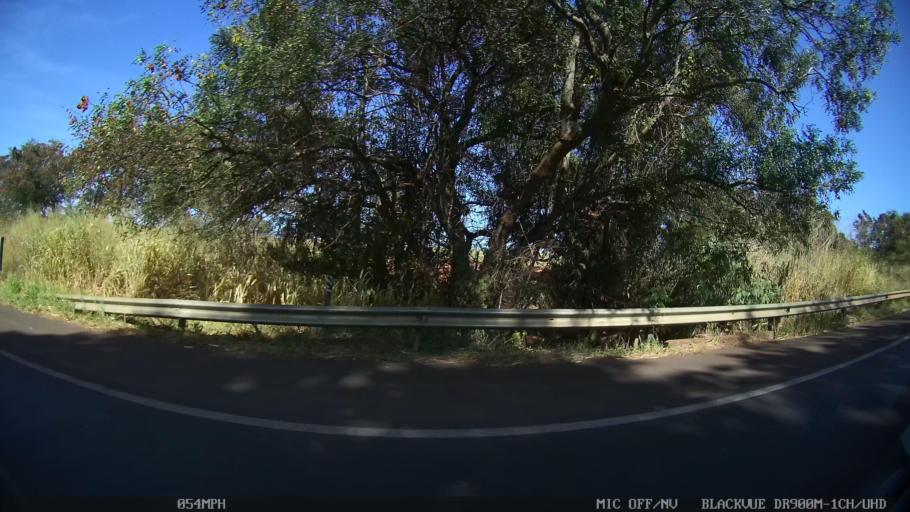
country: BR
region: Sao Paulo
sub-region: Olimpia
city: Olimpia
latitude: -20.6741
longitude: -48.8816
